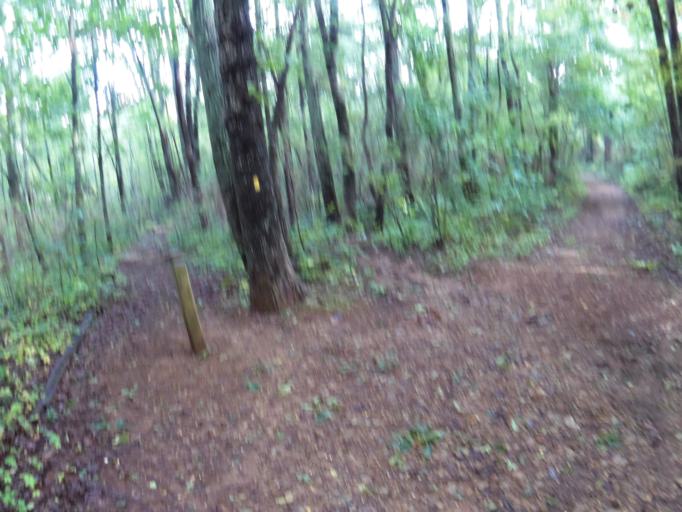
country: US
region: Virginia
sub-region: Rappahannock County
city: Washington
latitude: 38.7715
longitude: -78.2954
